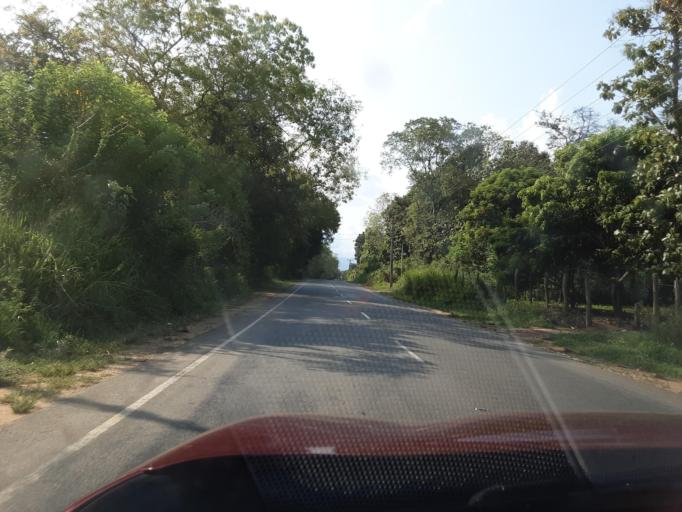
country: LK
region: Uva
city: Haputale
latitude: 6.6045
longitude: 81.1371
